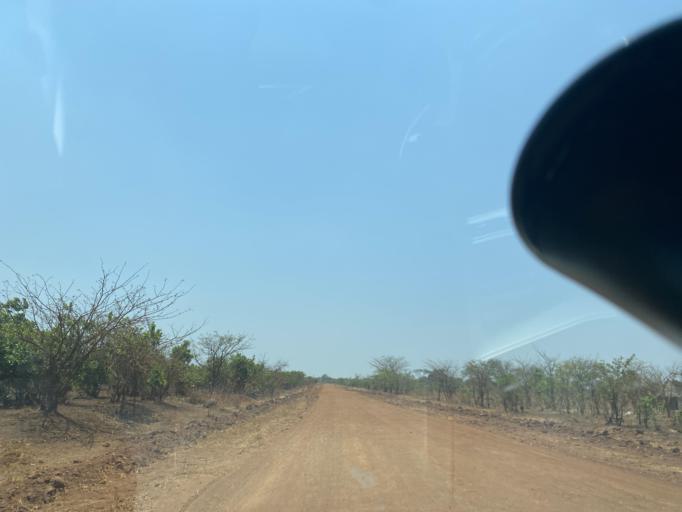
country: ZM
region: Lusaka
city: Lusaka
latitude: -15.4552
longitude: 27.9425
